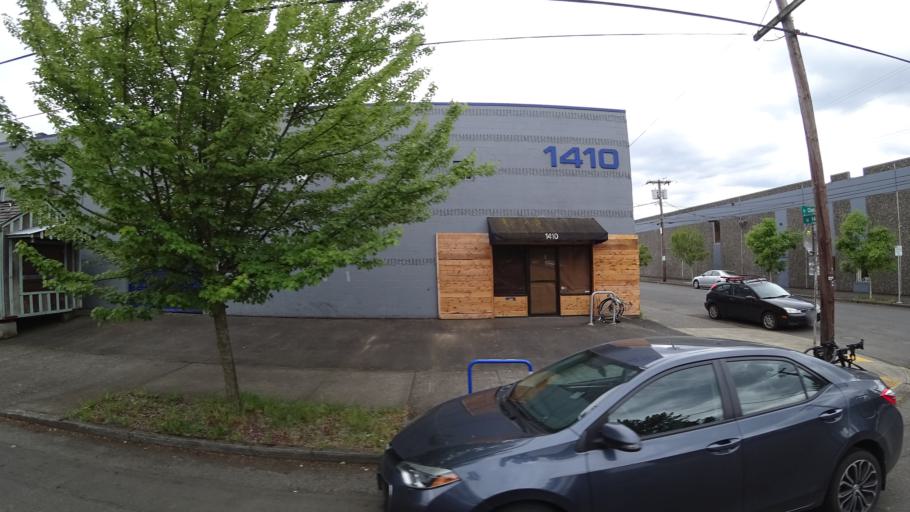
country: US
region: Oregon
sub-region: Multnomah County
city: Portland
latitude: 45.5035
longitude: -122.6516
